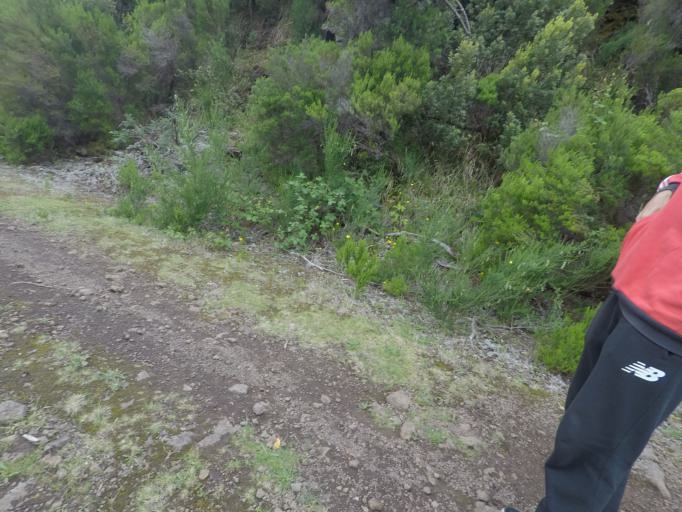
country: PT
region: Madeira
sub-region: Sao Vicente
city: Sao Vicente
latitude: 32.7724
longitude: -17.0559
